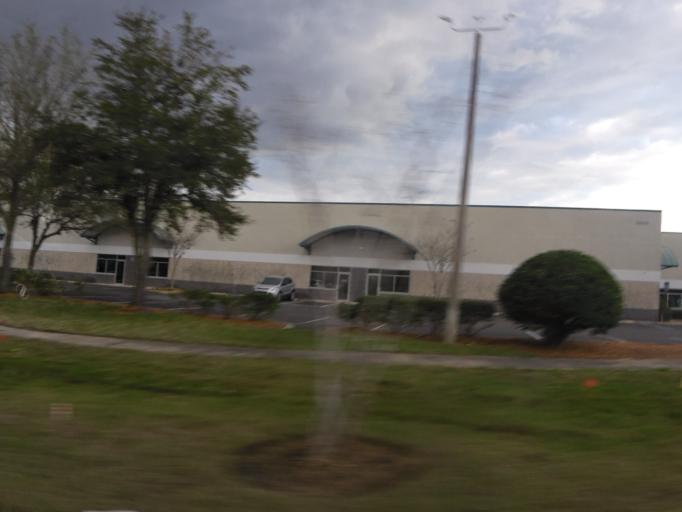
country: US
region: Florida
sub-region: Saint Johns County
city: Fruit Cove
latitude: 30.1860
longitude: -81.5739
